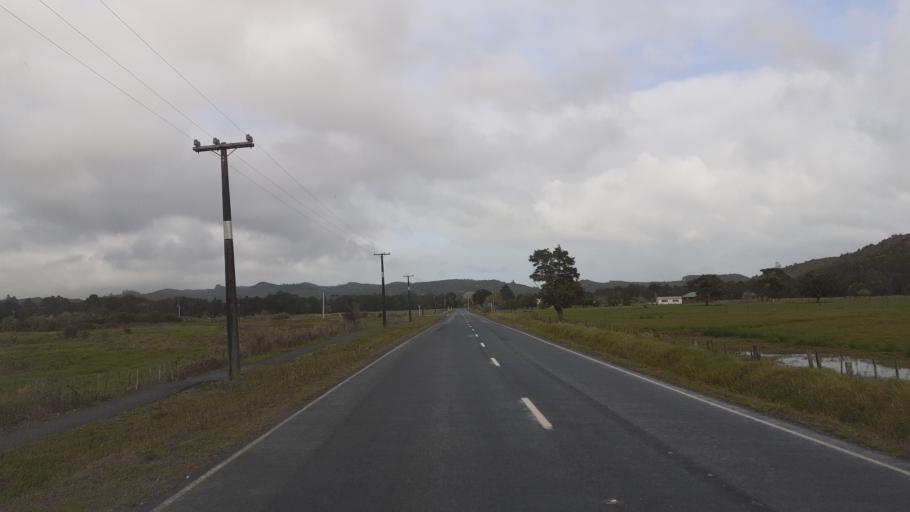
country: NZ
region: Northland
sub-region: Far North District
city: Moerewa
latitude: -35.3999
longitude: 173.9916
